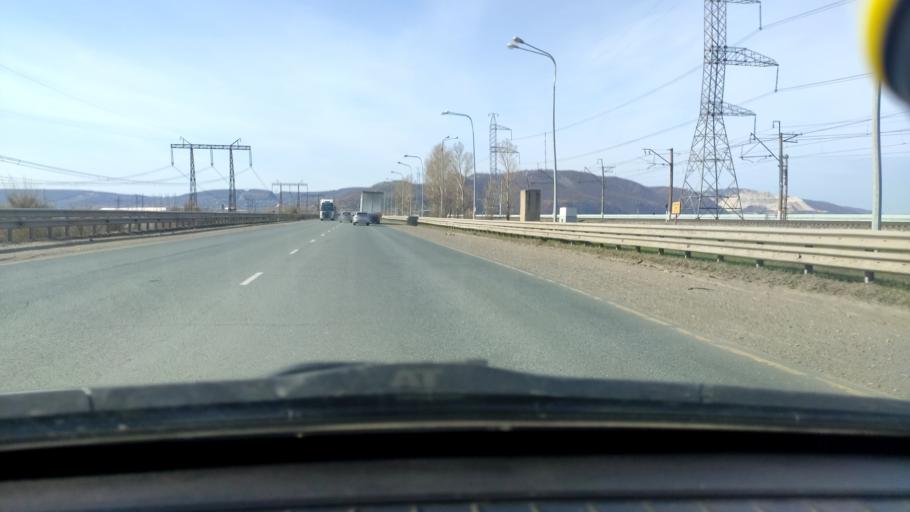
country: RU
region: Samara
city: Zhigulevsk
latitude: 53.4482
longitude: 49.4878
